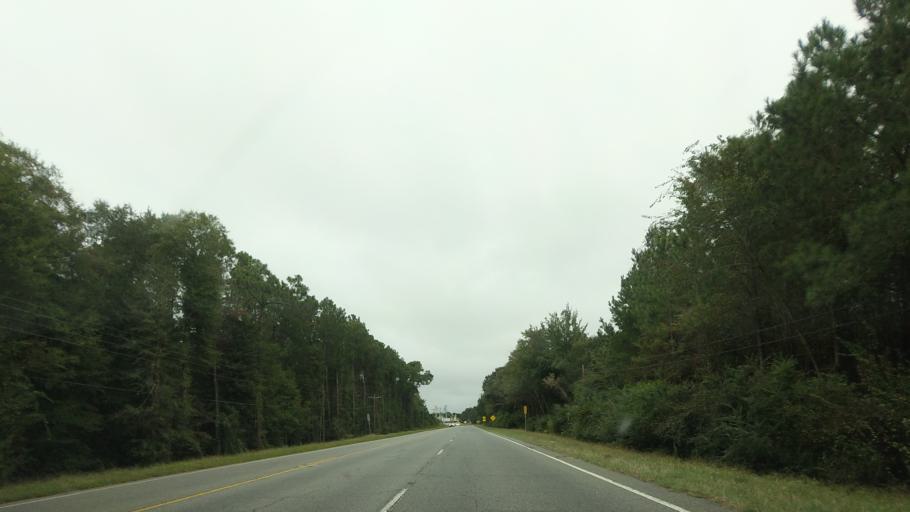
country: US
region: Georgia
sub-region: Irwin County
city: Ocilla
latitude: 31.6419
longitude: -83.2463
